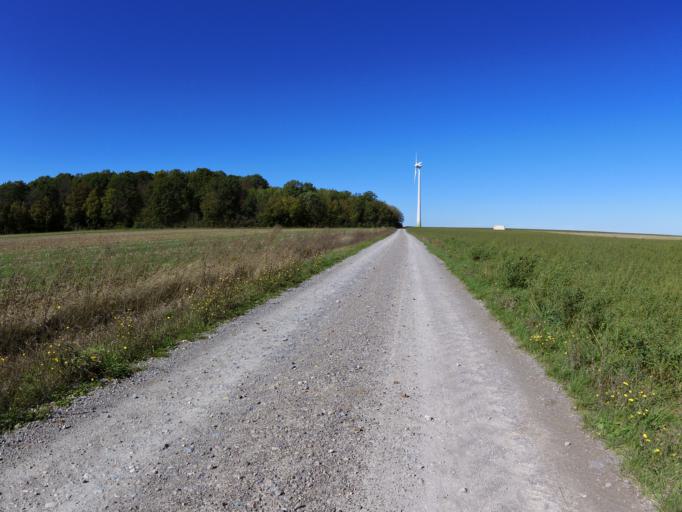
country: DE
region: Bavaria
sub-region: Regierungsbezirk Unterfranken
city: Theilheim
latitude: 49.7427
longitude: 10.0495
